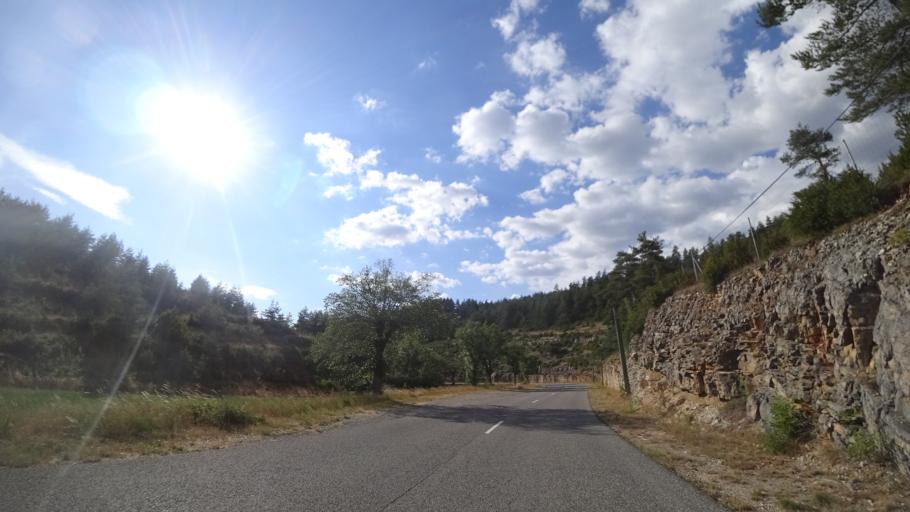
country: FR
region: Languedoc-Roussillon
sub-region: Departement de la Lozere
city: La Canourgue
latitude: 44.4063
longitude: 3.2873
